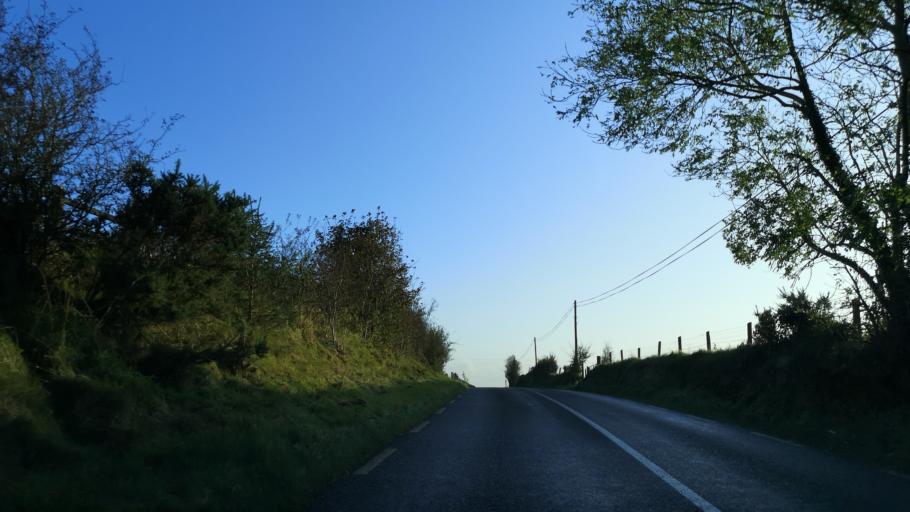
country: IE
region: Connaught
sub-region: Roscommon
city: Castlerea
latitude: 53.7014
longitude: -8.5682
